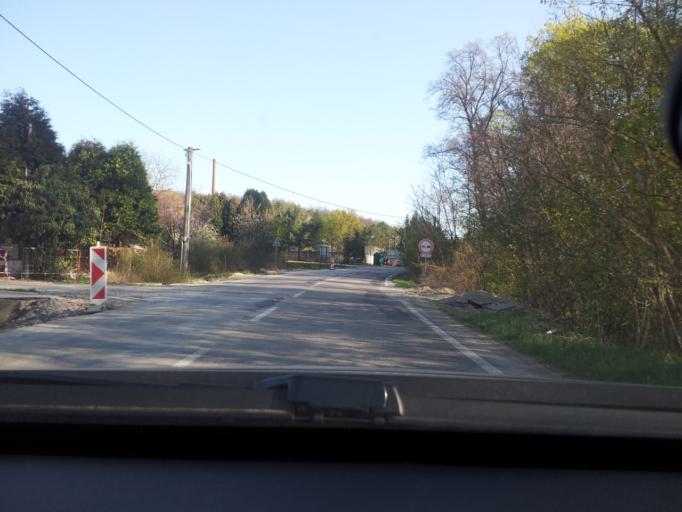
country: SK
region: Nitriansky
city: Zlate Moravce
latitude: 48.4309
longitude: 18.4113
